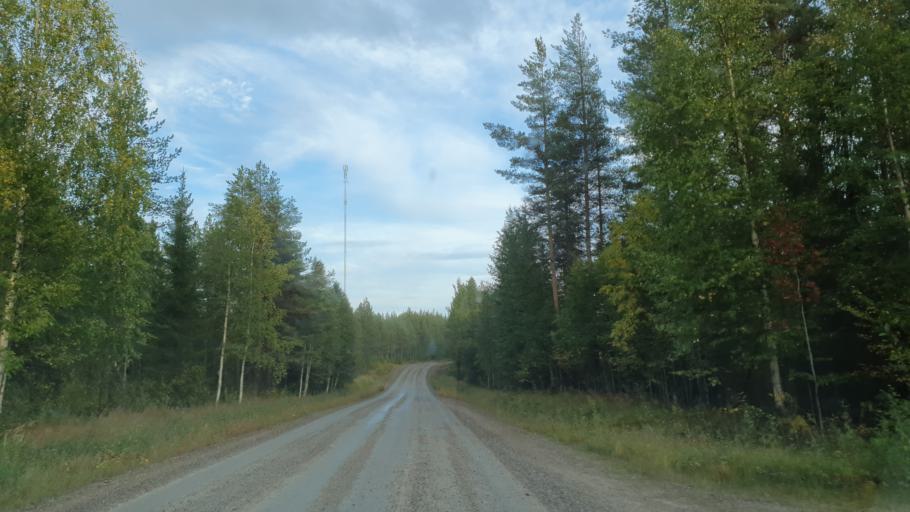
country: FI
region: Kainuu
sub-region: Kehys-Kainuu
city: Kuhmo
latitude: 64.4153
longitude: 29.5163
